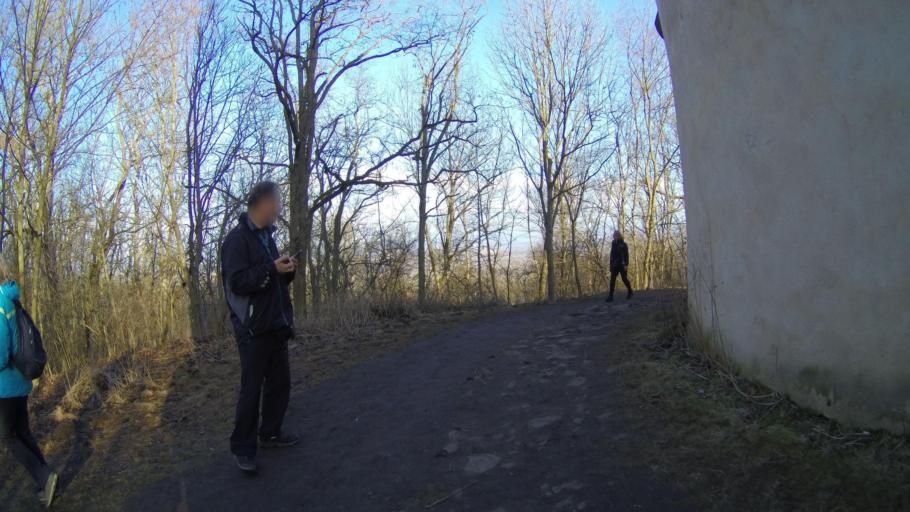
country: CZ
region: Ustecky
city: Roudnice nad Labem
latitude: 50.3865
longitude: 14.2895
